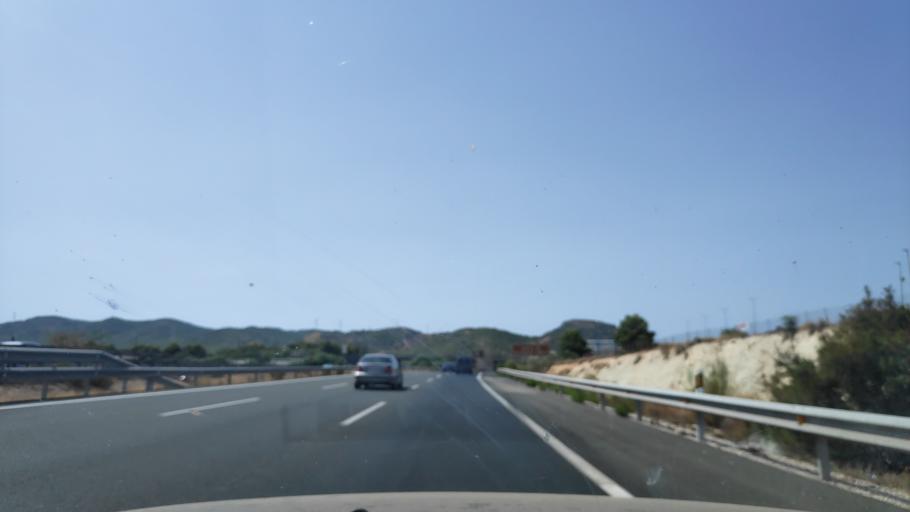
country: ES
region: Murcia
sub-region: Murcia
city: Murcia
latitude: 37.8836
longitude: -1.1359
